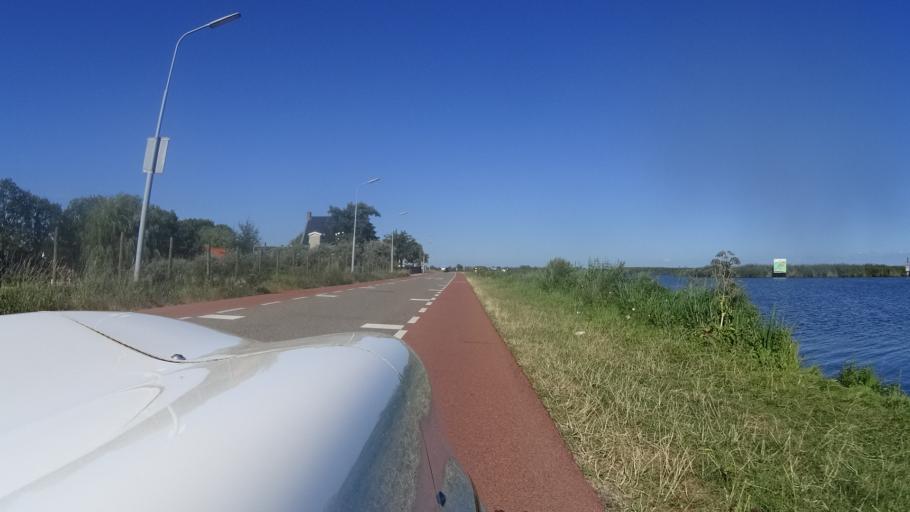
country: NL
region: South Holland
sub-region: Gemeente Kaag en Braassem
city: Leimuiden
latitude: 52.2333
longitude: 4.6743
